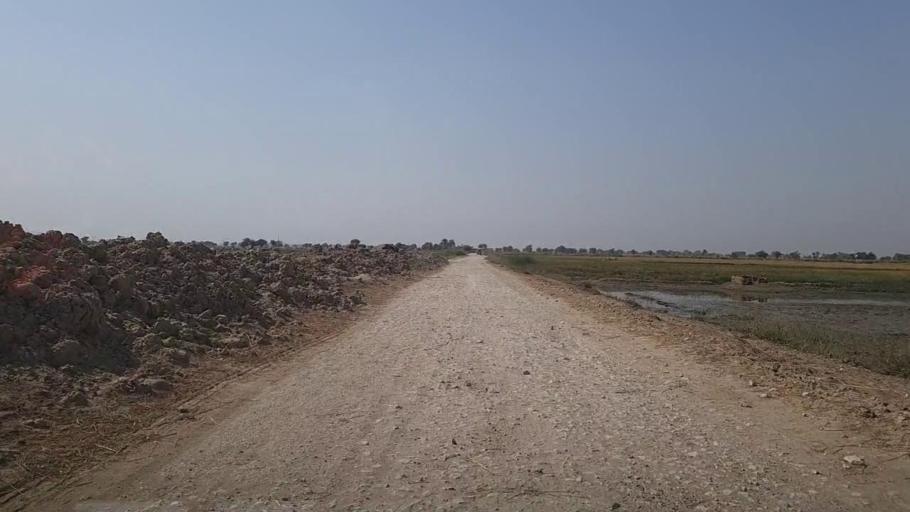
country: PK
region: Sindh
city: Kandhkot
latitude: 28.3926
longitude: 69.3089
